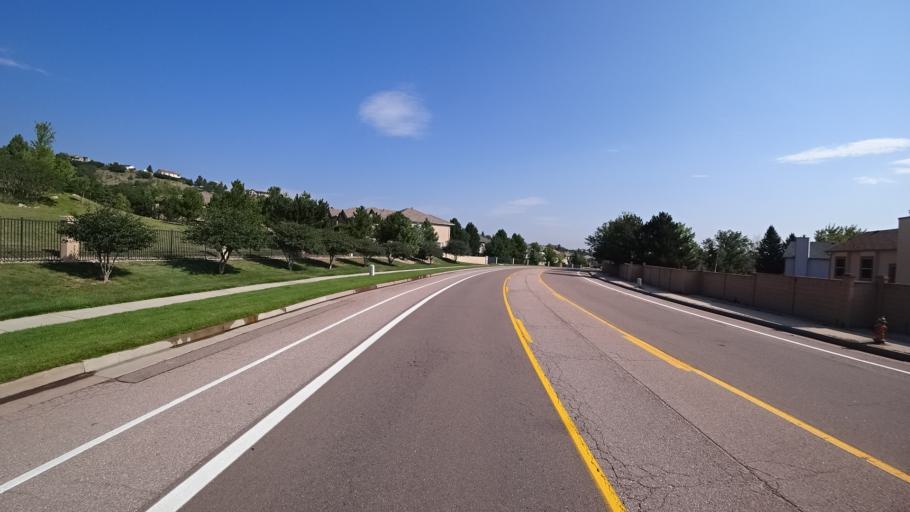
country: US
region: Colorado
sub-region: El Paso County
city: Fort Carson
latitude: 38.7638
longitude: -104.8186
